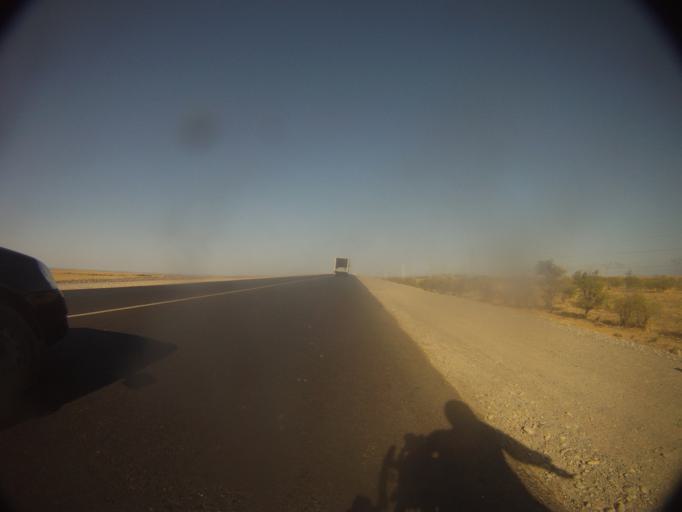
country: KZ
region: Zhambyl
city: Sarykemer
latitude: 42.9797
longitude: 71.5769
